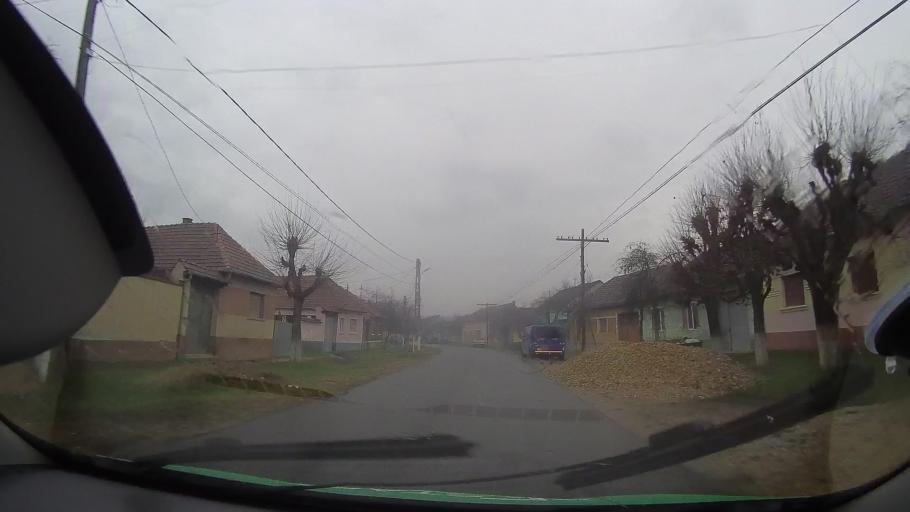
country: RO
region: Bihor
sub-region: Comuna Uileacu de Beius
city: Uileacu de Beius
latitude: 46.6815
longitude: 22.2246
